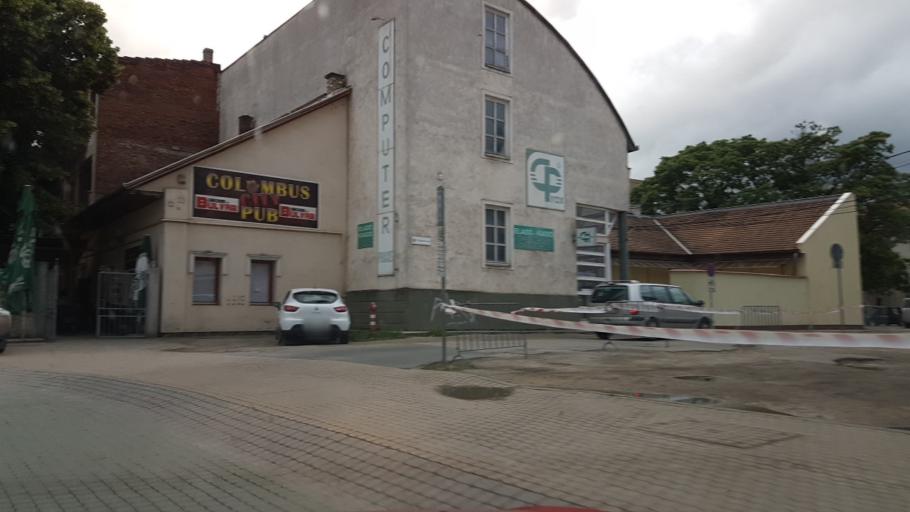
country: HU
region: Borsod-Abauj-Zemplen
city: Miskolc
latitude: 48.1034
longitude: 20.7875
